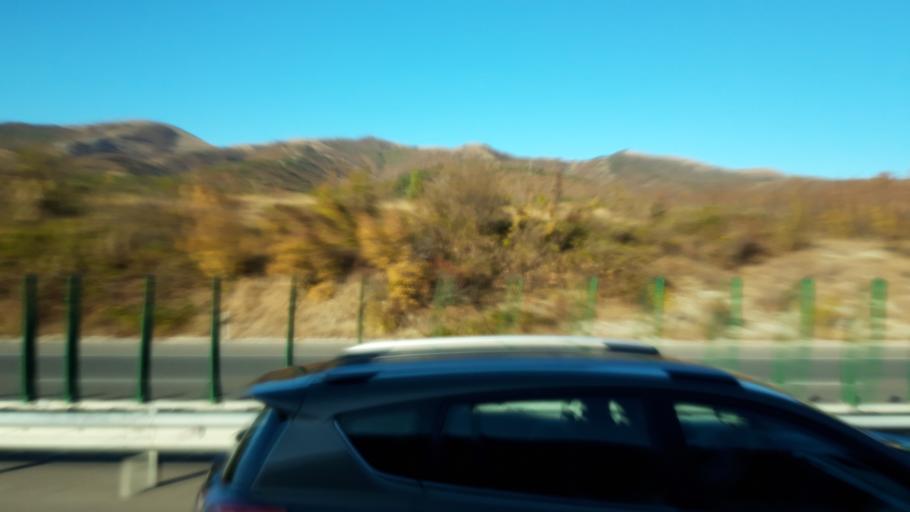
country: RU
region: Krasnodarskiy
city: Kabardinka
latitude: 44.6420
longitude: 37.9743
